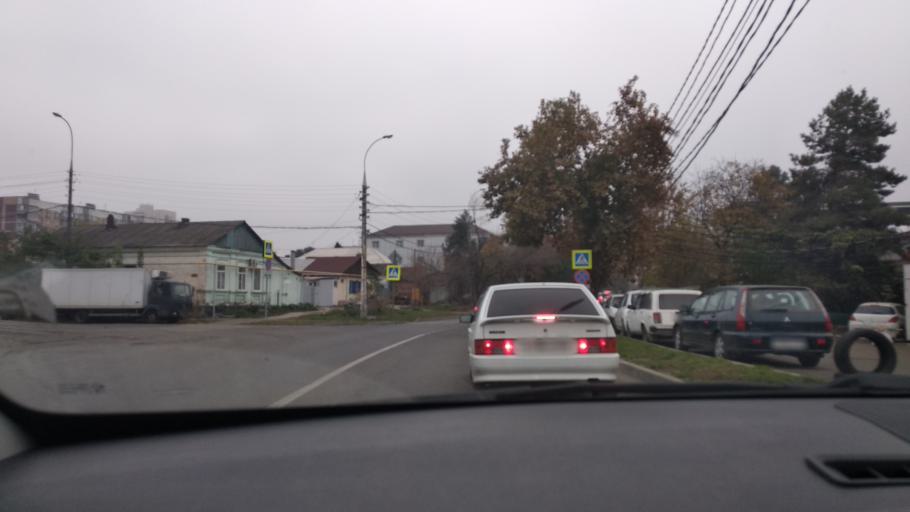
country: RU
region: Krasnodarskiy
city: Krasnodar
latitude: 45.0232
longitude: 39.0094
